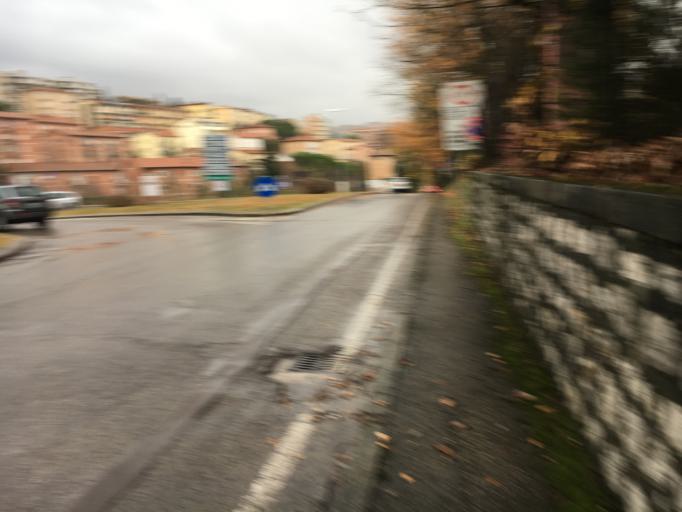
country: IT
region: Umbria
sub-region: Provincia di Perugia
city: Perugia
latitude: 43.1180
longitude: 12.3717
